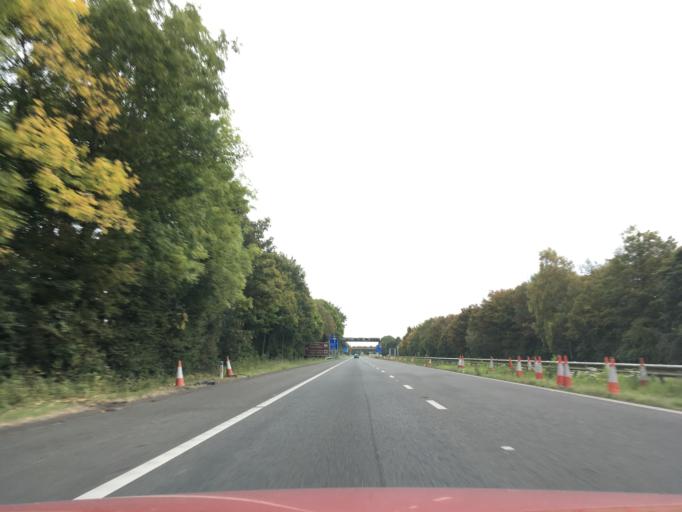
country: GB
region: Wales
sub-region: Monmouthshire
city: Chepstow
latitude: 51.6183
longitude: -2.6912
